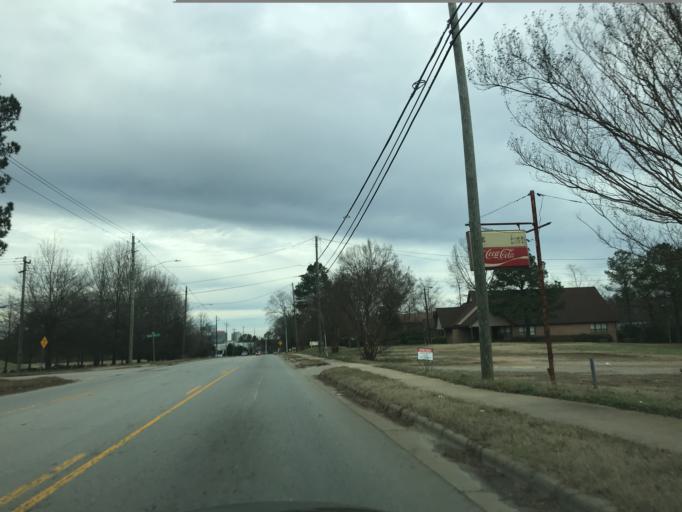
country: US
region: North Carolina
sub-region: Wake County
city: Raleigh
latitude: 35.7461
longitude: -78.6314
